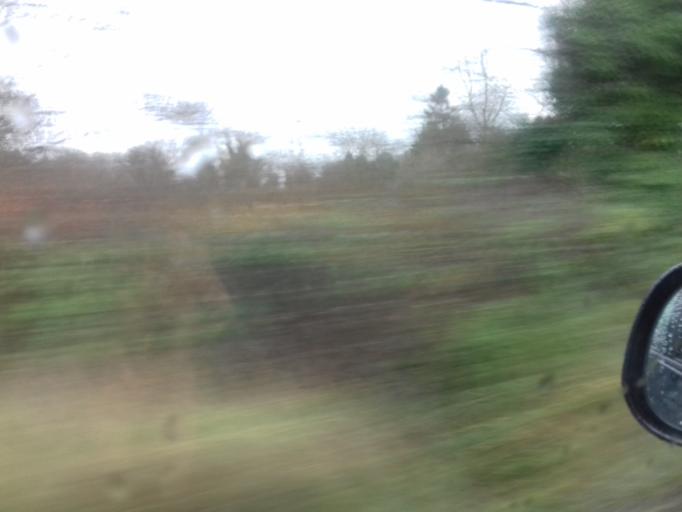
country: IE
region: Leinster
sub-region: Kilkenny
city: Graiguenamanagh
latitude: 52.5917
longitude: -6.9690
